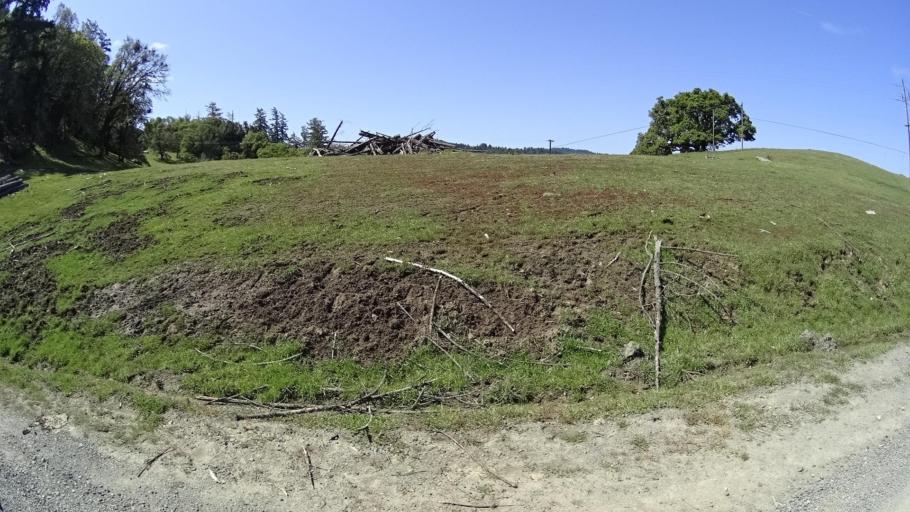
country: US
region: California
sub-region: Humboldt County
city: Redway
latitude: 40.0213
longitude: -123.6261
